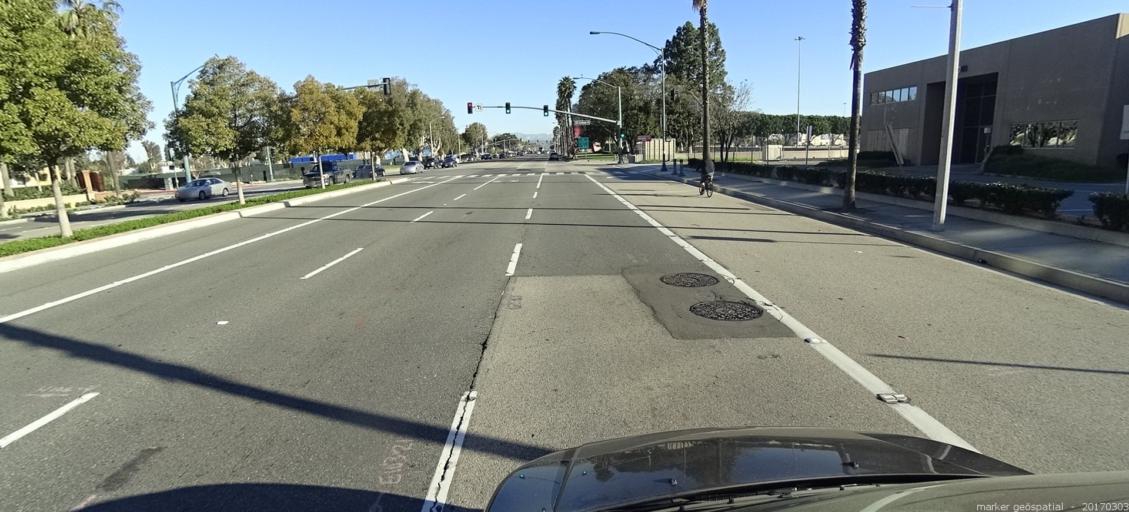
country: US
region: California
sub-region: Orange County
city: Orange
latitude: 33.7973
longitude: -117.8891
